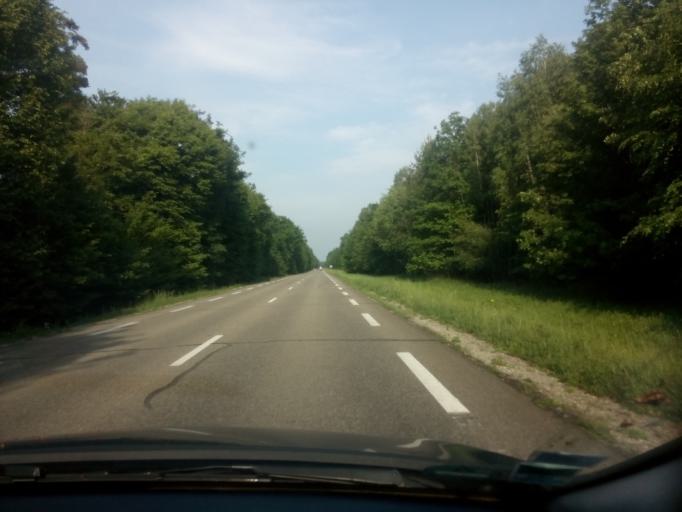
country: FR
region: Alsace
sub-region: Departement du Bas-Rhin
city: Oberhoffen-sur-Moder
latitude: 48.8348
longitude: 7.8816
